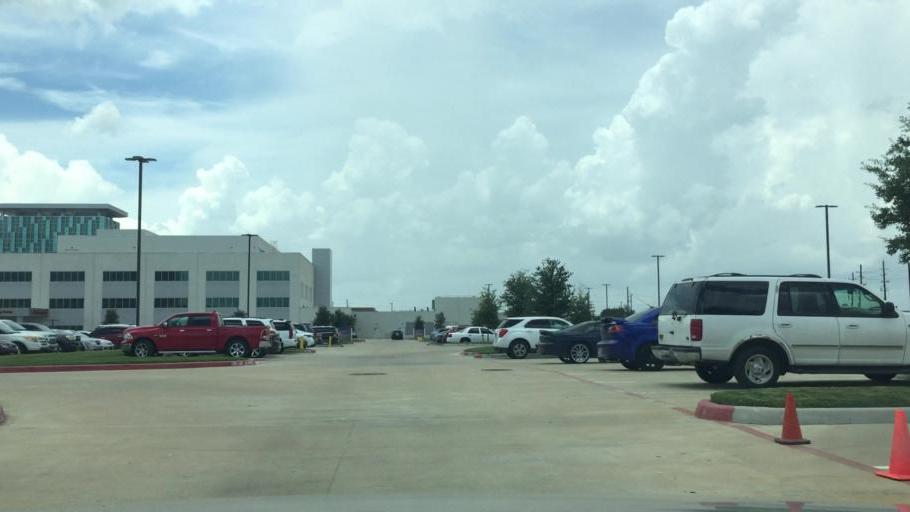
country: US
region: Texas
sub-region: Harris County
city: Cypress
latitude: 29.9868
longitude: -95.7307
